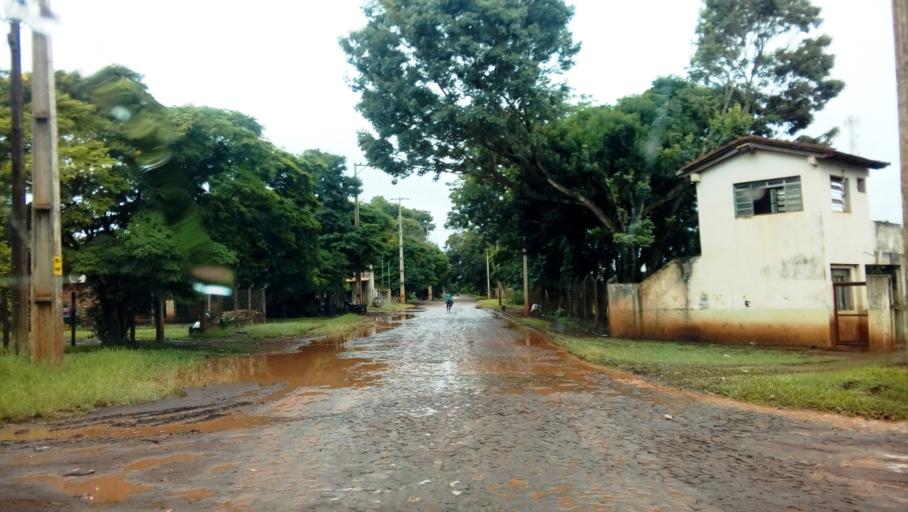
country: PY
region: Alto Parana
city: Ciudad del Este
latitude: -25.4207
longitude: -54.6397
